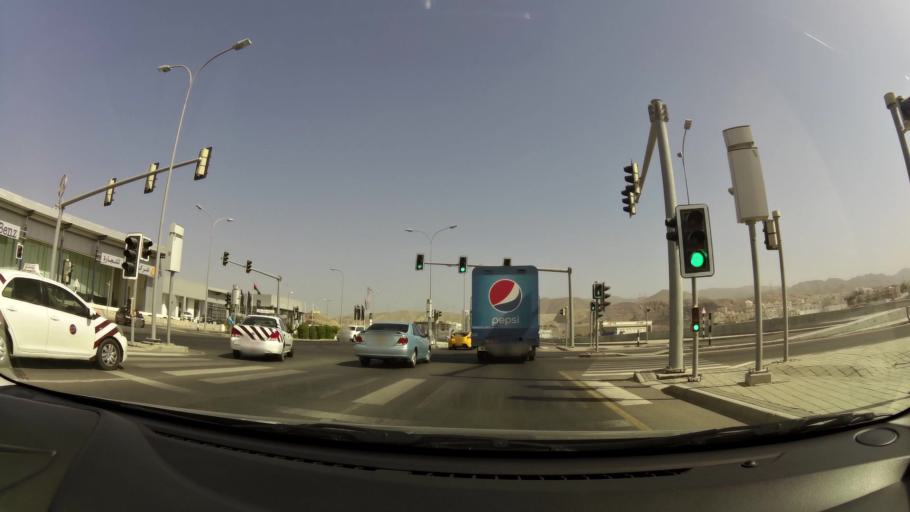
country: OM
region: Muhafazat Masqat
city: Muscat
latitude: 23.6108
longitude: 58.4992
